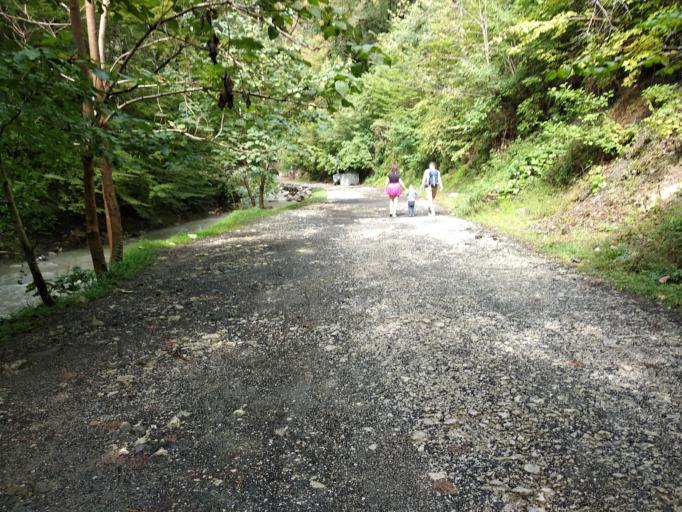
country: RU
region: Krasnodarskiy
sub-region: Sochi City
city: Sochi
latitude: 43.6348
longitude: 39.8176
